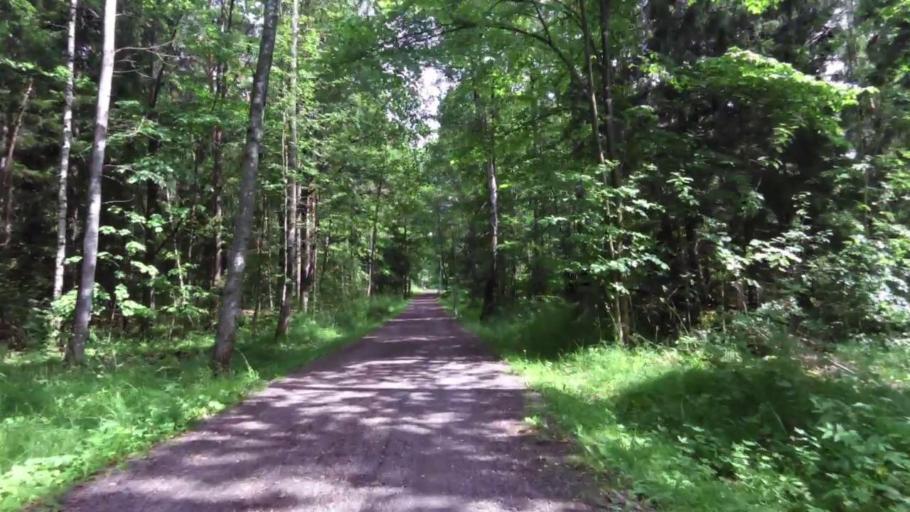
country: SE
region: OEstergoetland
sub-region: Linkopings Kommun
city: Linkoping
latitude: 58.4090
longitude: 15.5792
